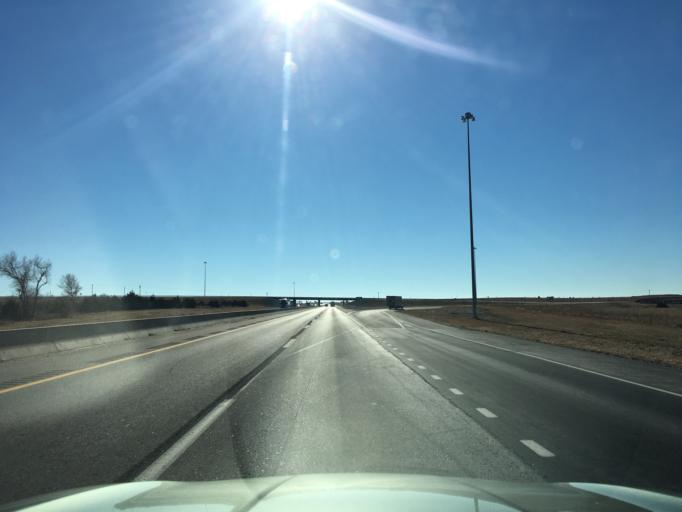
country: US
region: Kansas
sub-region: Sumner County
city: Wellington
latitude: 37.0613
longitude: -97.3385
